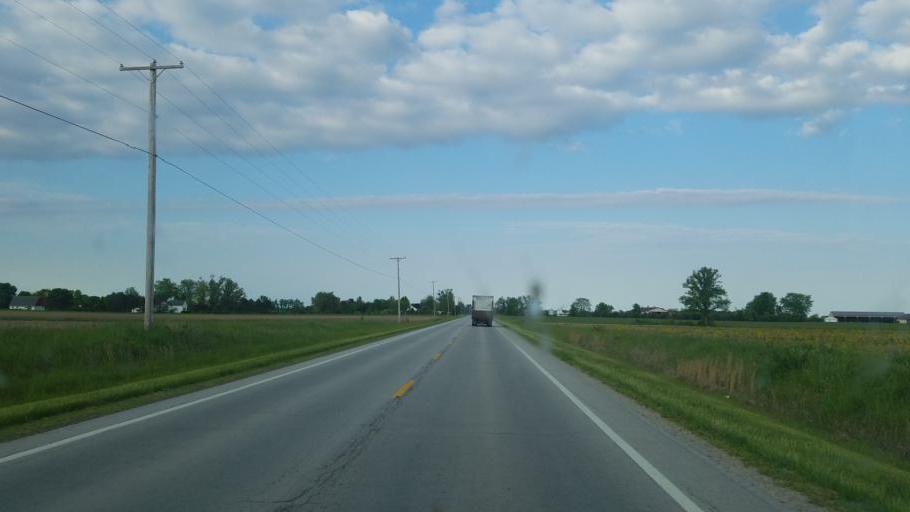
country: US
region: Ohio
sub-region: Madison County
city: Bethel
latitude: 39.6401
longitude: -83.3403
